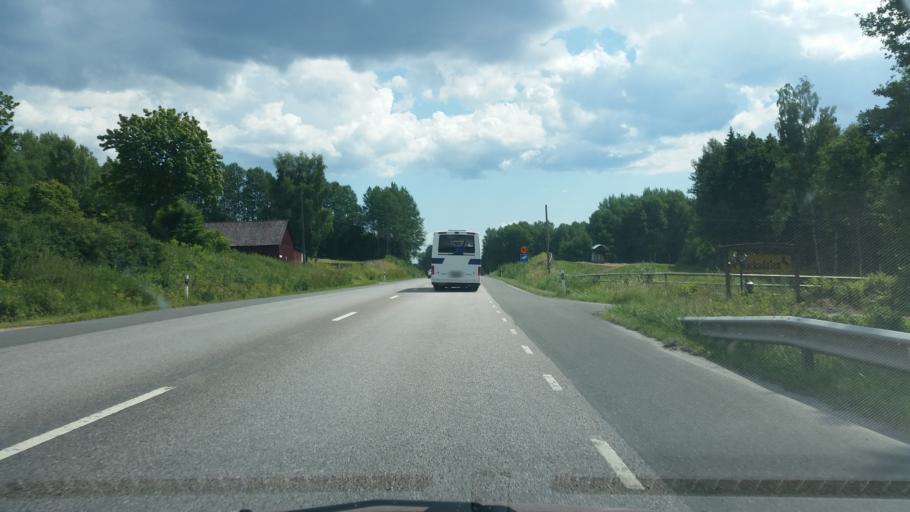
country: SE
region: Vaestra Goetaland
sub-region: Skovde Kommun
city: Skoevde
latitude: 58.3902
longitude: 13.7885
